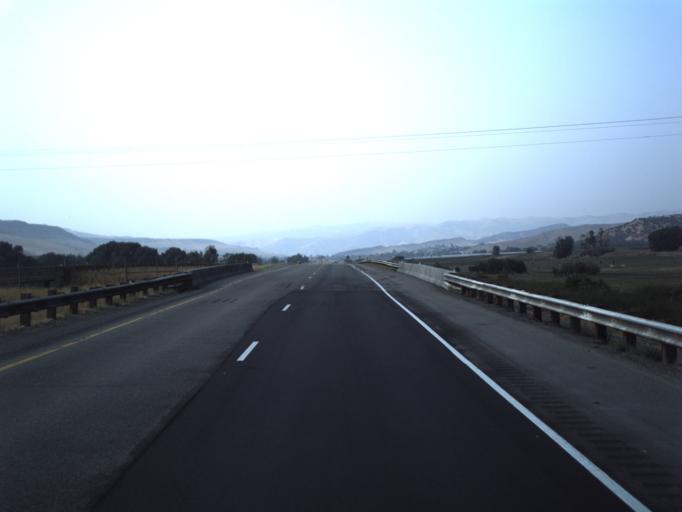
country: US
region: Utah
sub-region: Summit County
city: Coalville
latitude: 40.8736
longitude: -111.3902
